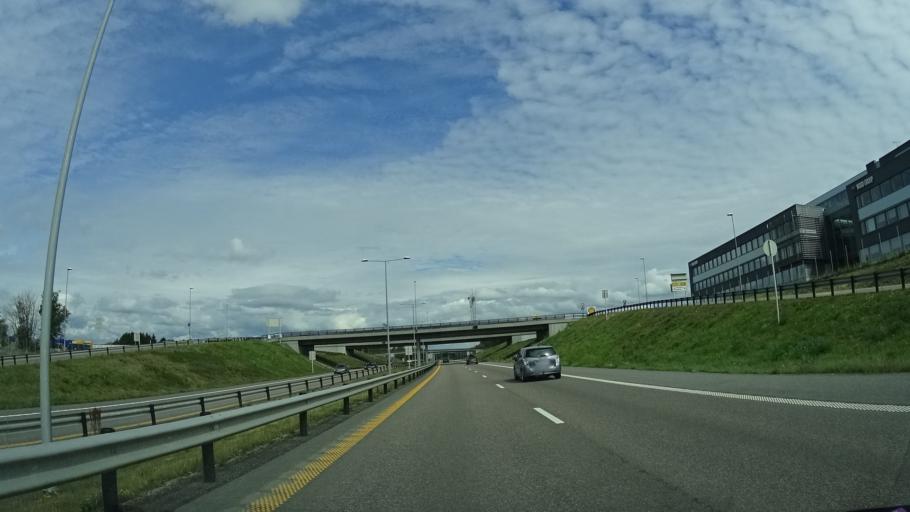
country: NO
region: Vestfold
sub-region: Sandefjord
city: Sandefjord
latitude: 59.1750
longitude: 10.2073
